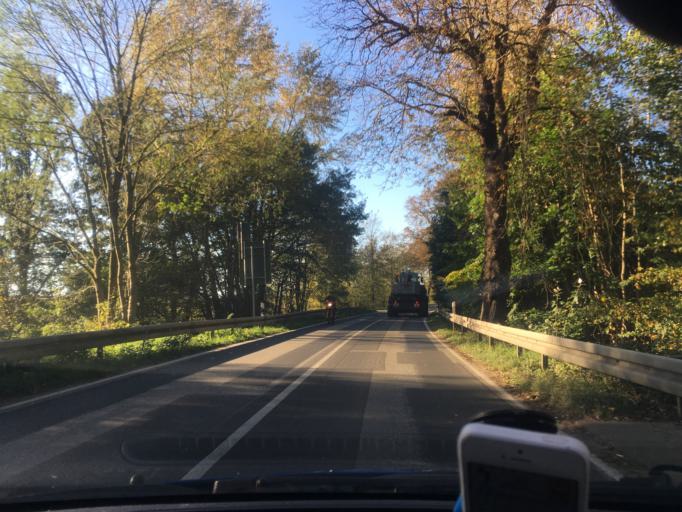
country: DE
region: Mecklenburg-Vorpommern
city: Zarrentin
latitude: 53.5329
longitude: 10.9457
